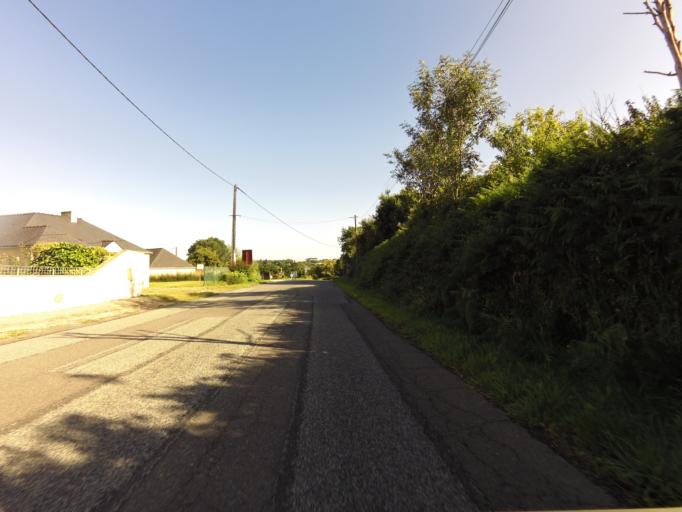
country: FR
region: Brittany
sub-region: Departement du Morbihan
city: Limerzel
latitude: 47.6319
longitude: -2.3542
